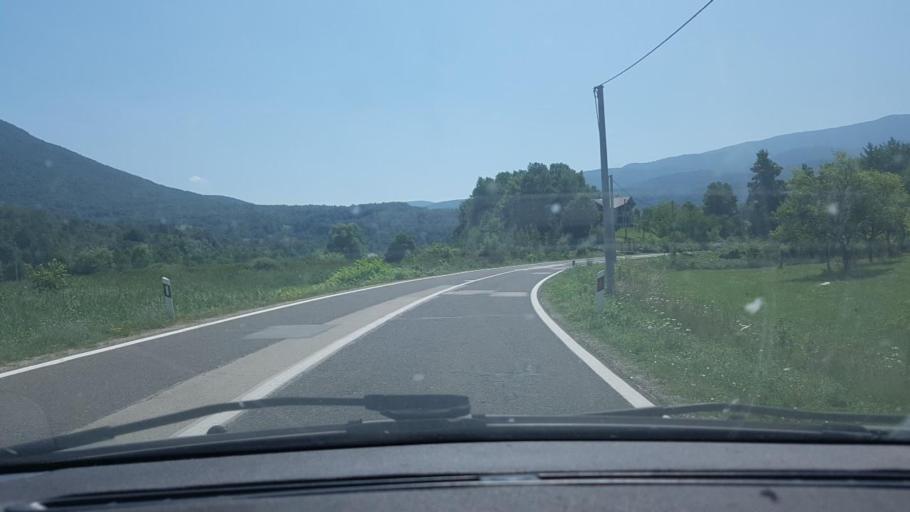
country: BA
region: Federation of Bosnia and Herzegovina
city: Bihac
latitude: 44.7555
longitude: 15.9452
